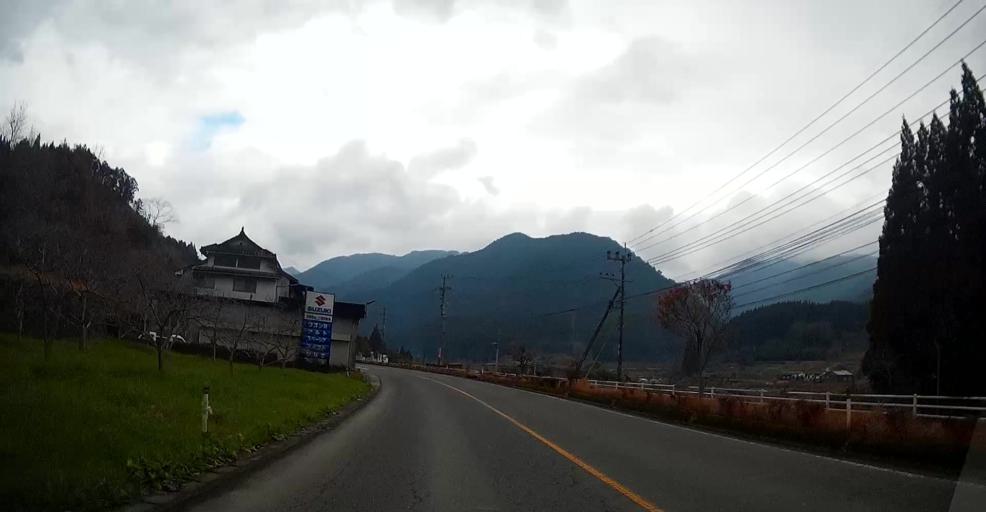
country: JP
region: Kumamoto
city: Matsubase
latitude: 32.6170
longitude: 130.8381
